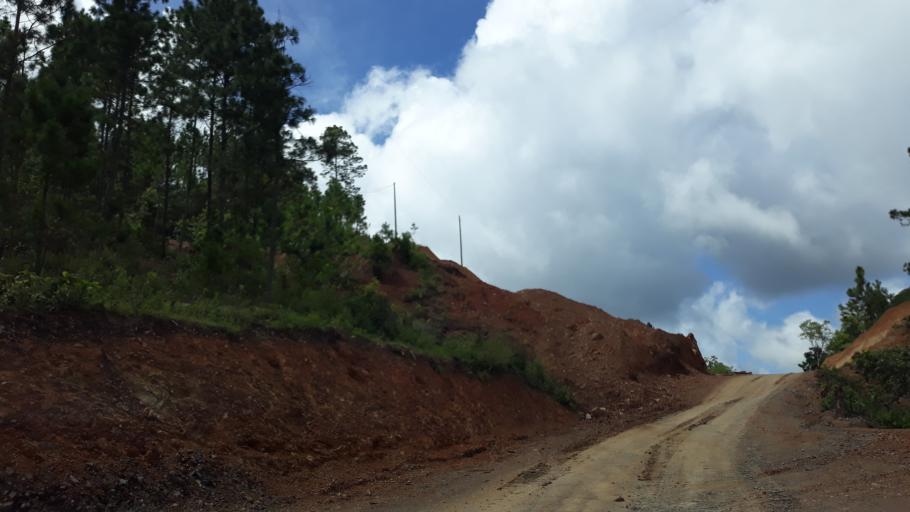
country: HN
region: El Paraiso
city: Santa Cruz
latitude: 13.7626
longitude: -86.6478
